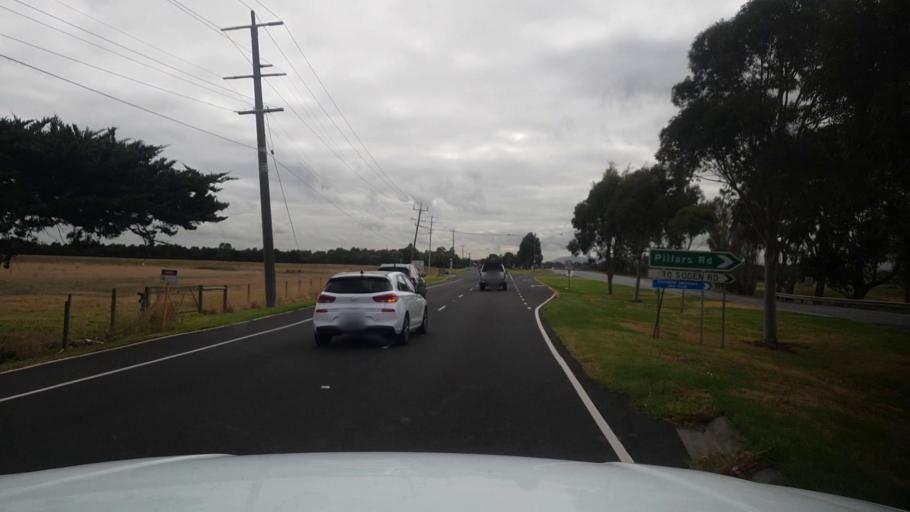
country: AU
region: Victoria
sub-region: Kingston
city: Waterways
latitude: -38.0232
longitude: 145.1355
